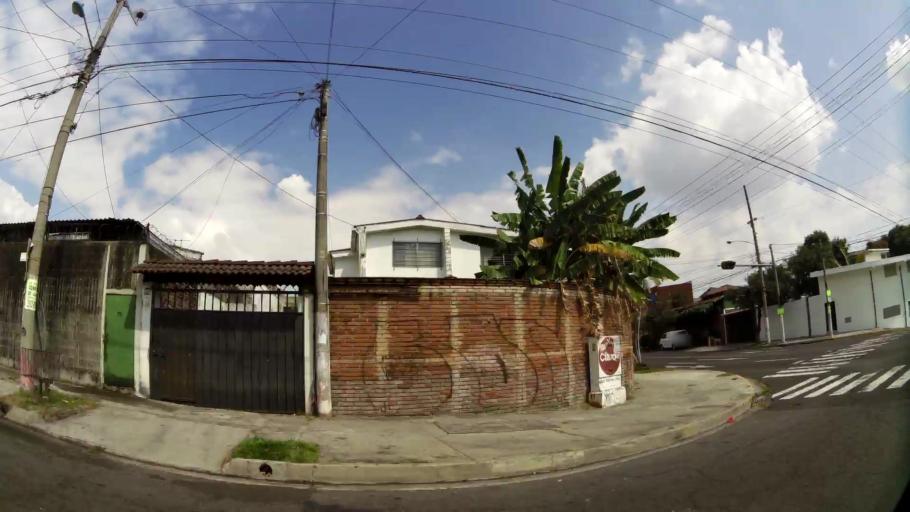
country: SV
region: San Salvador
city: Mejicanos
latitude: 13.7099
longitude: -89.2199
